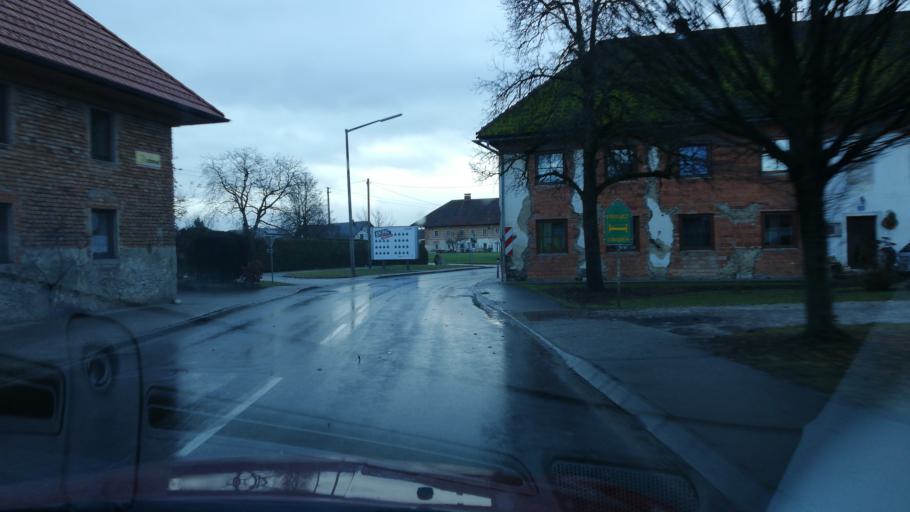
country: AT
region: Upper Austria
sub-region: Wels-Land
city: Sattledt
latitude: 48.0098
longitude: 14.0626
